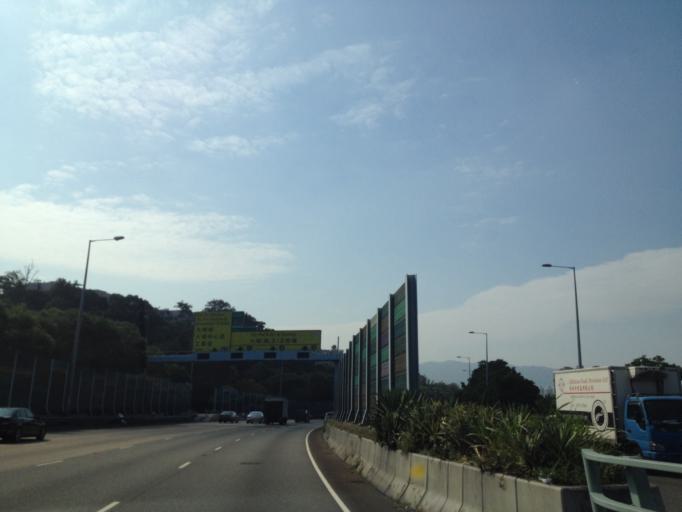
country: HK
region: Tai Po
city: Tai Po
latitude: 22.4391
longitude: 114.1883
